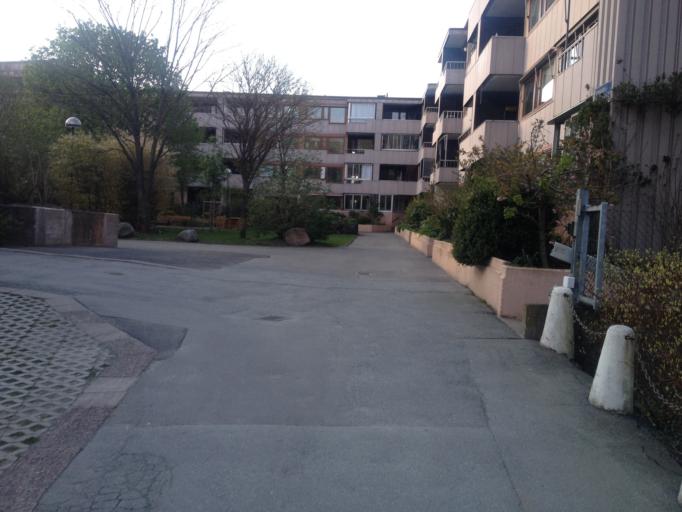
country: SE
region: Vaestra Goetaland
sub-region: Goteborg
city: Goeteborg
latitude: 57.6971
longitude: 11.9423
